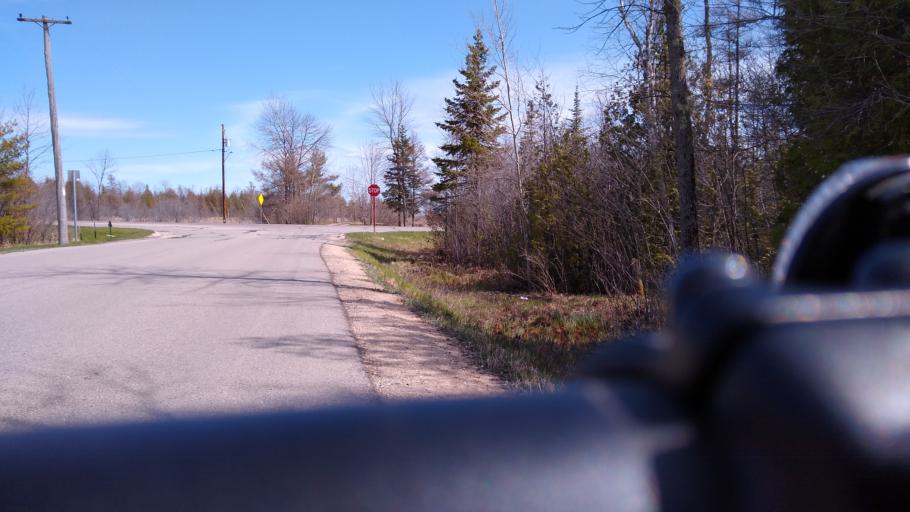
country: US
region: Michigan
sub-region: Delta County
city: Escanaba
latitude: 45.6764
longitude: -87.1460
